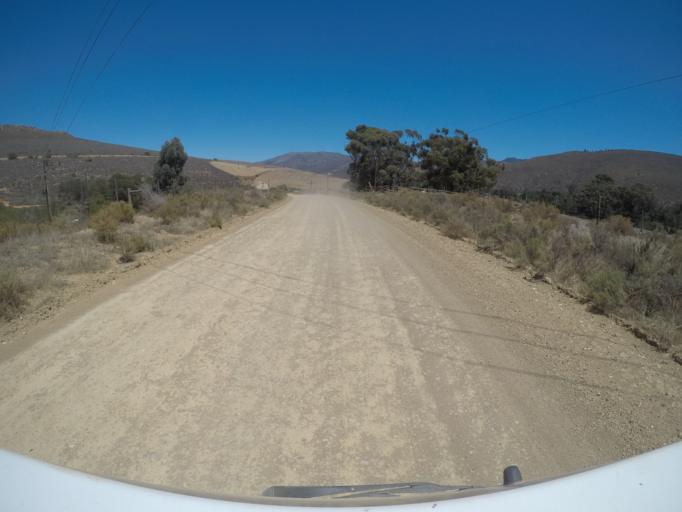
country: ZA
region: Western Cape
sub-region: Overberg District Municipality
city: Caledon
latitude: -34.1470
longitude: 19.2463
